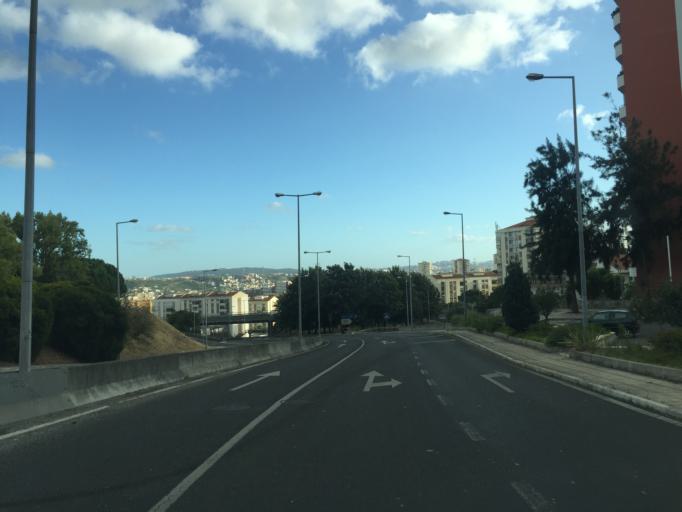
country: PT
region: Lisbon
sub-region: Odivelas
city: Ramada
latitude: 38.8035
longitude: -9.1863
